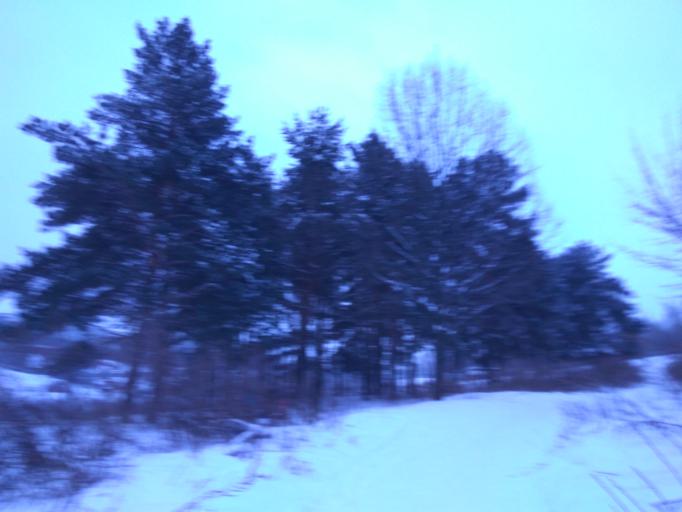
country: RU
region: Moscow
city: Orekhovo-Borisovo
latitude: 55.5979
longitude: 37.7086
